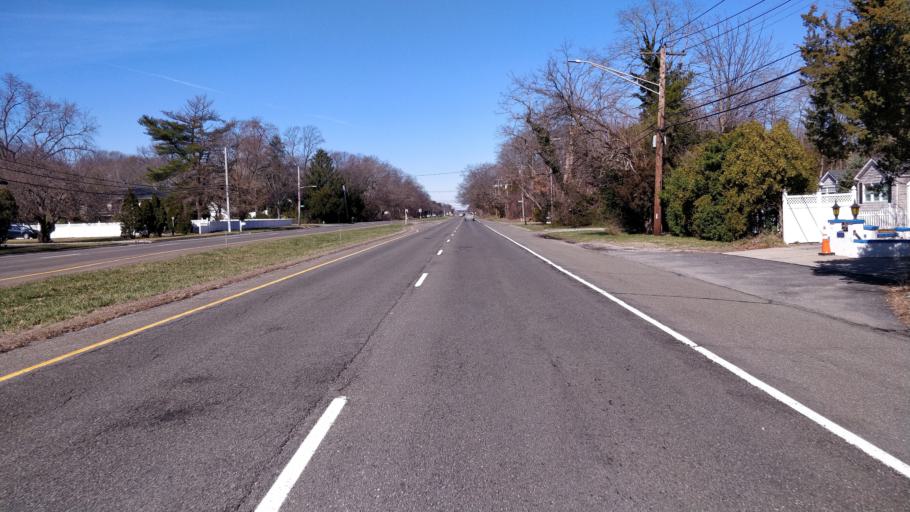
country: US
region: New York
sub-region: Suffolk County
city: Commack
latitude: 40.8346
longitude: -73.2655
